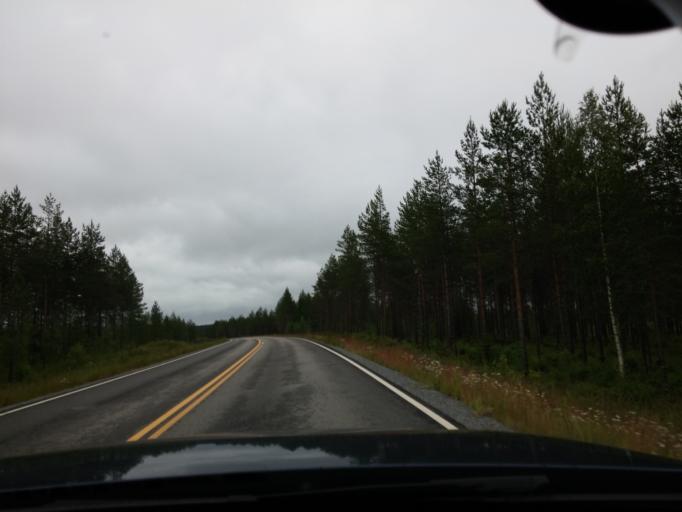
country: FI
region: Central Finland
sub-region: Saarijaervi-Viitasaari
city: Pylkoenmaeki
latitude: 62.6403
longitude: 24.8516
